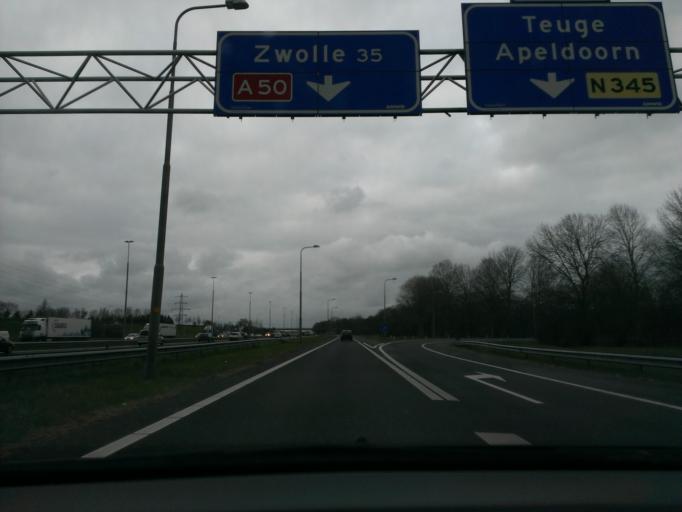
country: NL
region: Gelderland
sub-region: Gemeente Apeldoorn
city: Apeldoorn
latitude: 52.2081
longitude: 6.0221
